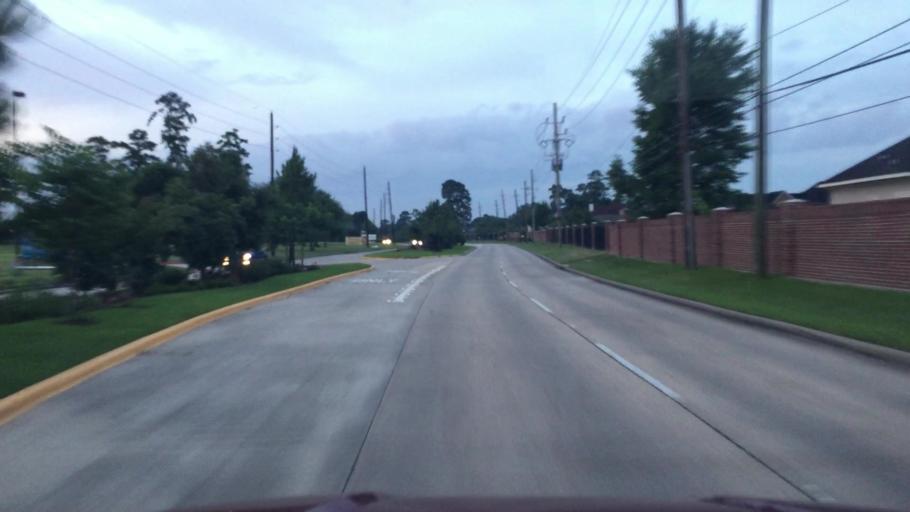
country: US
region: Texas
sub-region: Harris County
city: Tomball
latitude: 30.0365
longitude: -95.5361
